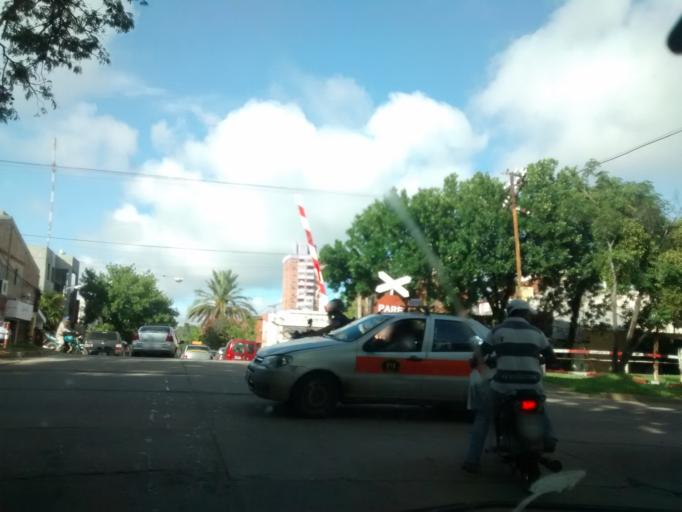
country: AR
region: Chaco
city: Resistencia
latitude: -27.4541
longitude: -58.9916
